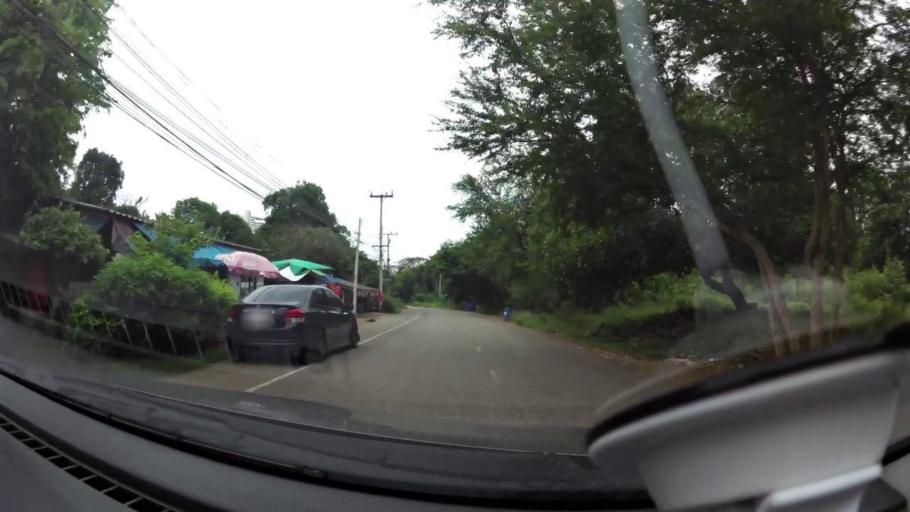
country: TH
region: Prachuap Khiri Khan
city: Pran Buri
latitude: 12.4359
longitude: 99.9743
